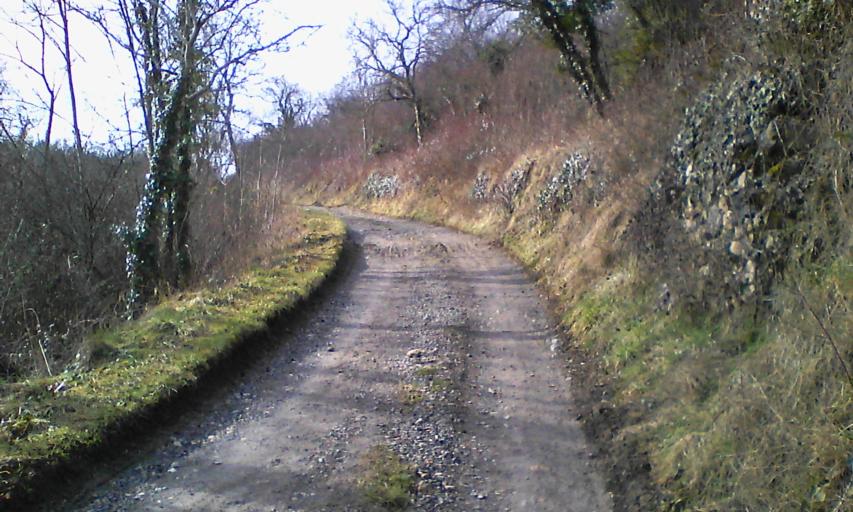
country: FR
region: Auvergne
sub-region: Departement du Puy-de-Dome
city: Ceyrat
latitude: 45.7424
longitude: 3.0721
